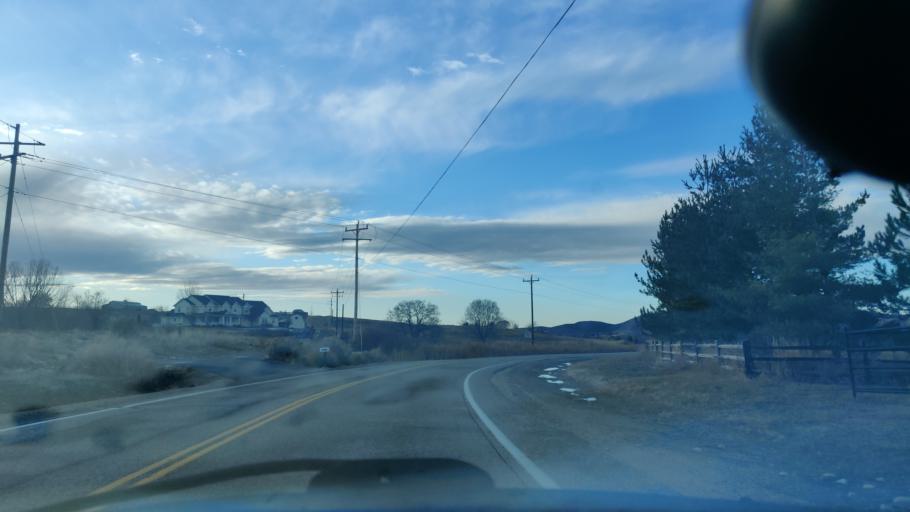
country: US
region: Idaho
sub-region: Ada County
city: Eagle
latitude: 43.7279
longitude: -116.2601
